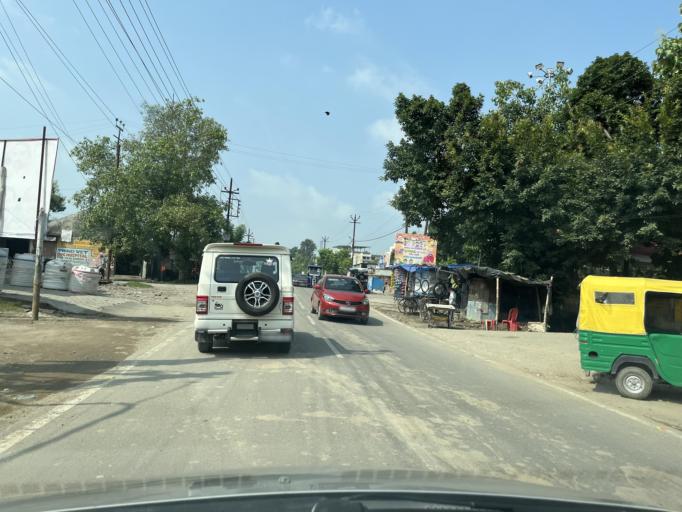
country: IN
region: Uttarakhand
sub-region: Udham Singh Nagar
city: Bazpur
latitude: 29.1634
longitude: 79.1569
